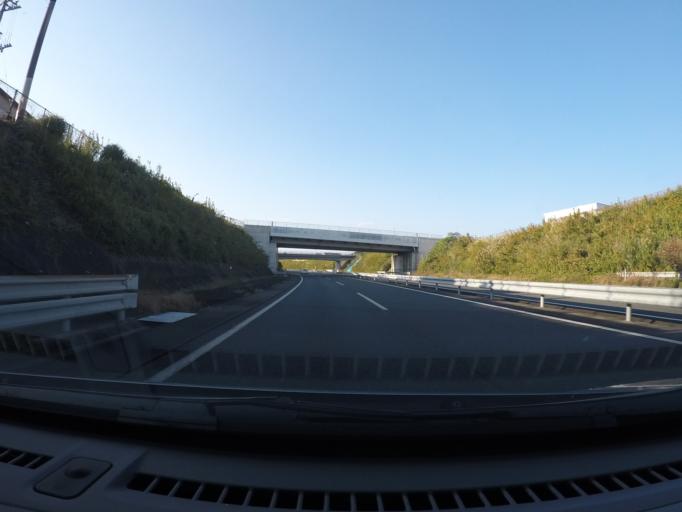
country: JP
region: Kagoshima
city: Kajiki
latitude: 31.8149
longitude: 130.7063
